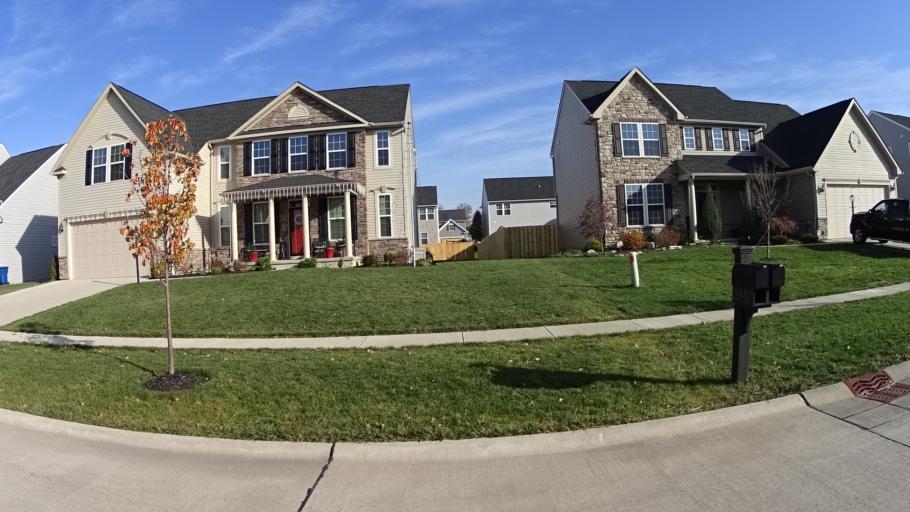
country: US
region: Ohio
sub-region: Lorain County
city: Avon
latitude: 41.4534
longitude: -82.0579
